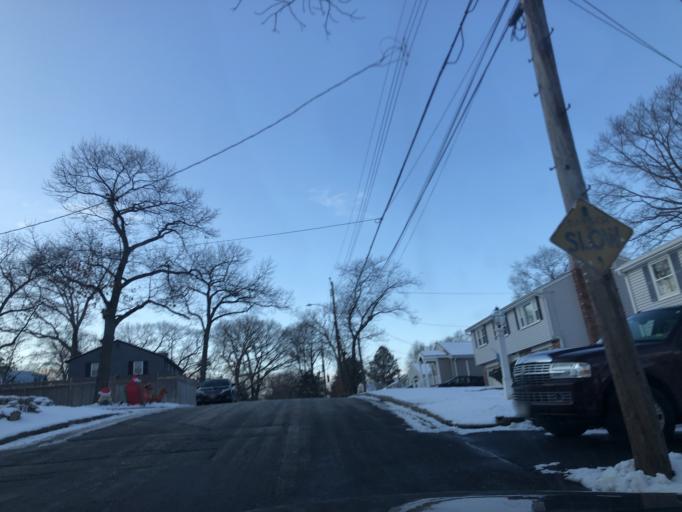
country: US
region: Massachusetts
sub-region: Middlesex County
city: Arlington
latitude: 42.4256
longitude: -71.1609
